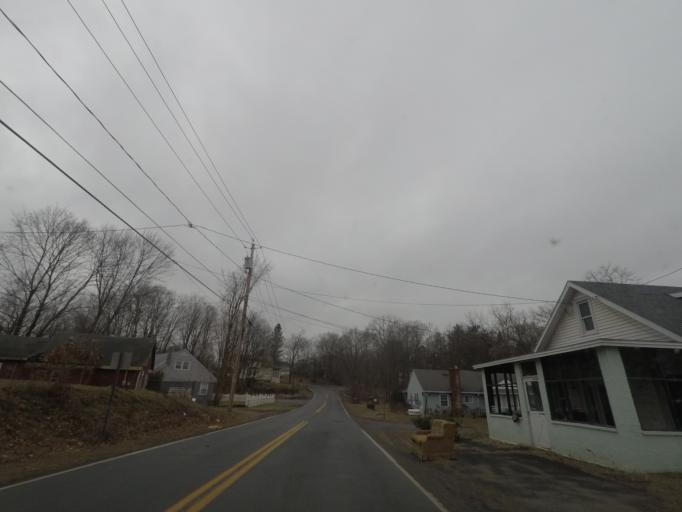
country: US
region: New York
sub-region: Saratoga County
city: Waterford
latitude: 42.7972
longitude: -73.6653
